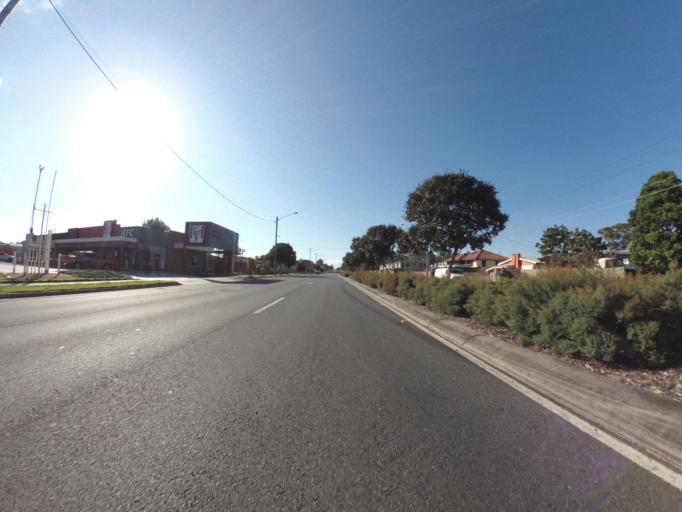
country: AU
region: Queensland
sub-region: Brisbane
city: Belmont
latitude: -27.4745
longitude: 153.1215
